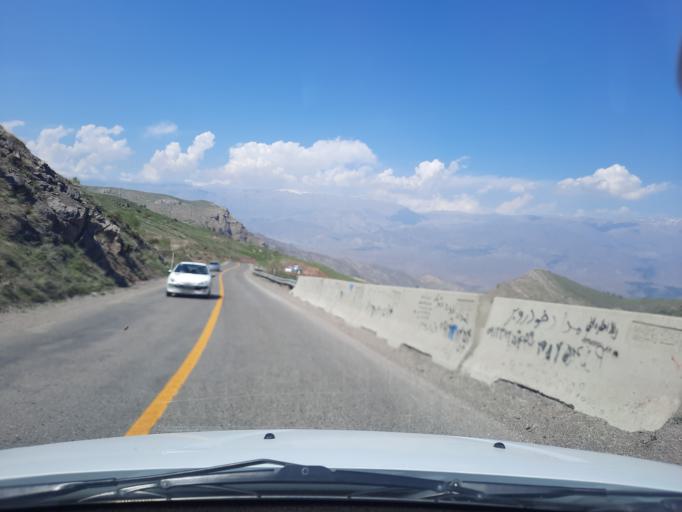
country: IR
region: Qazvin
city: Qazvin
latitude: 36.4040
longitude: 50.2256
